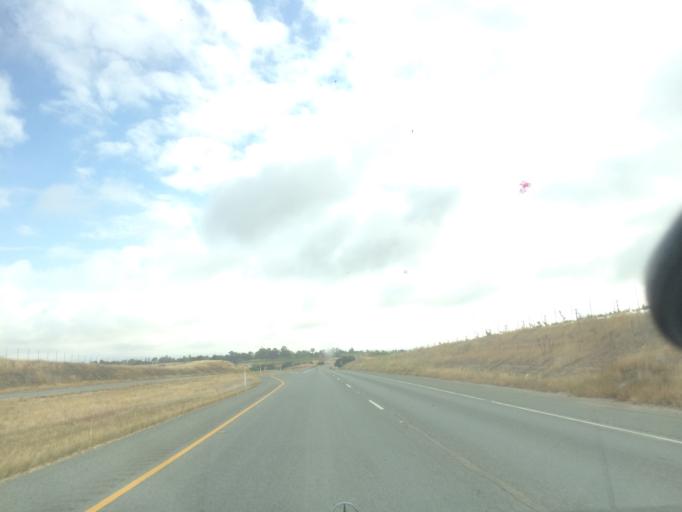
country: US
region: California
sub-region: San Luis Obispo County
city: Paso Robles
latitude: 35.6538
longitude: -120.6174
